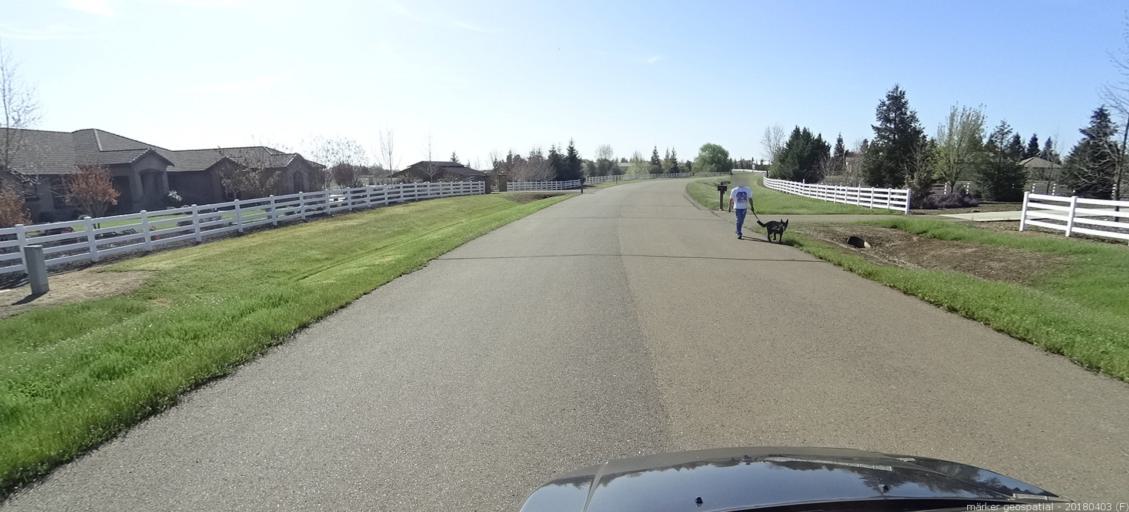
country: US
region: California
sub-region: Sacramento County
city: Clay
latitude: 38.4142
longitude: -121.1886
